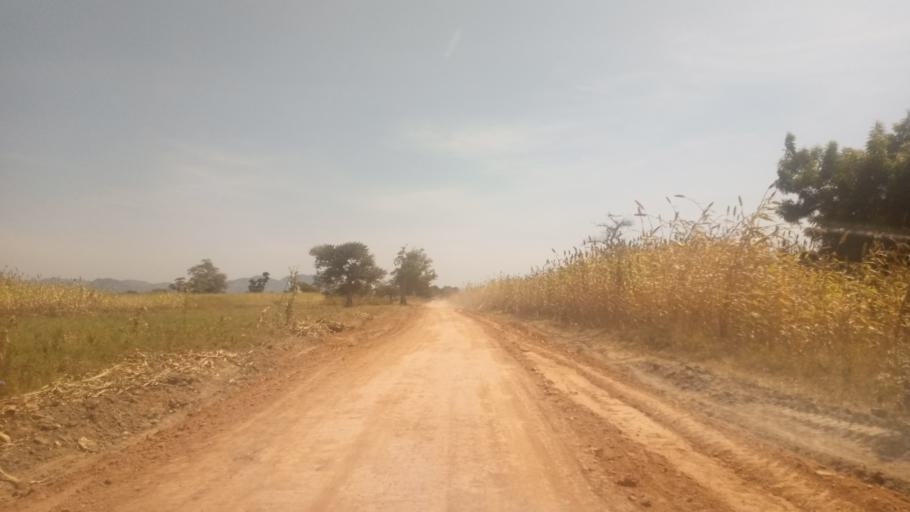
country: NG
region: Adamawa
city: Madagali
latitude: 10.8463
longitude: 13.3939
